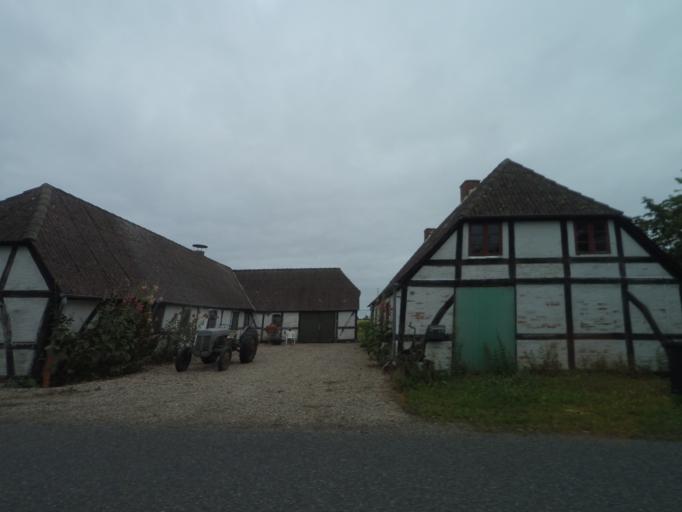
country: DK
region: South Denmark
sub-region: Nordfyns Kommune
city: Otterup
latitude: 55.5634
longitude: 10.4251
